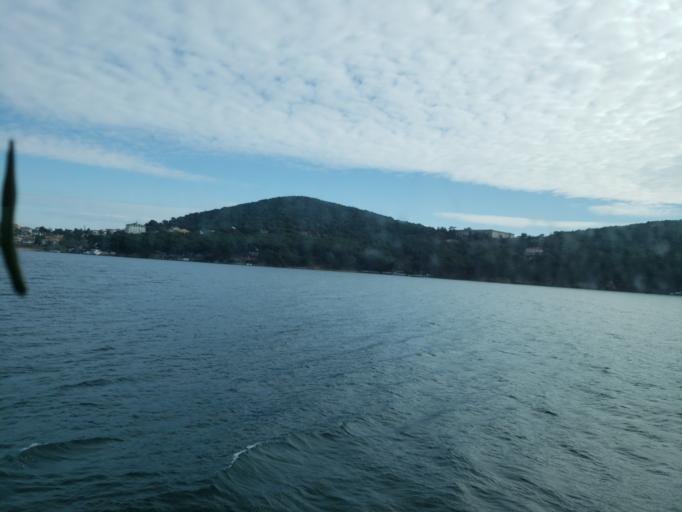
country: TR
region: Istanbul
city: Adalan
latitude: 40.8821
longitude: 29.0818
